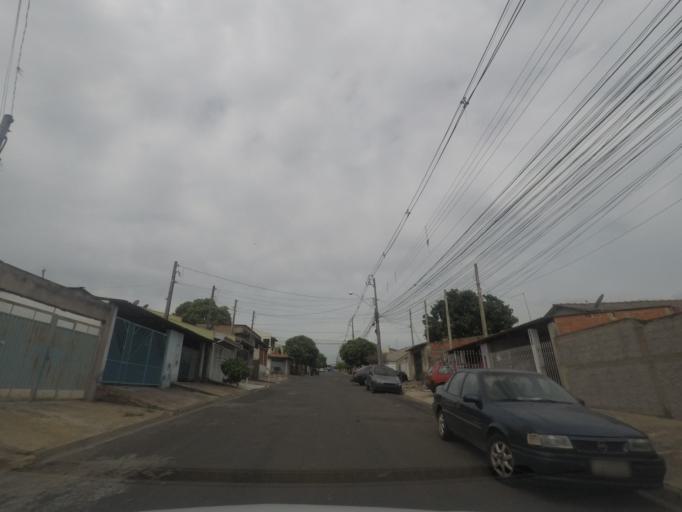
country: BR
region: Sao Paulo
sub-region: Sumare
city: Sumare
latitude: -22.8029
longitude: -47.2785
